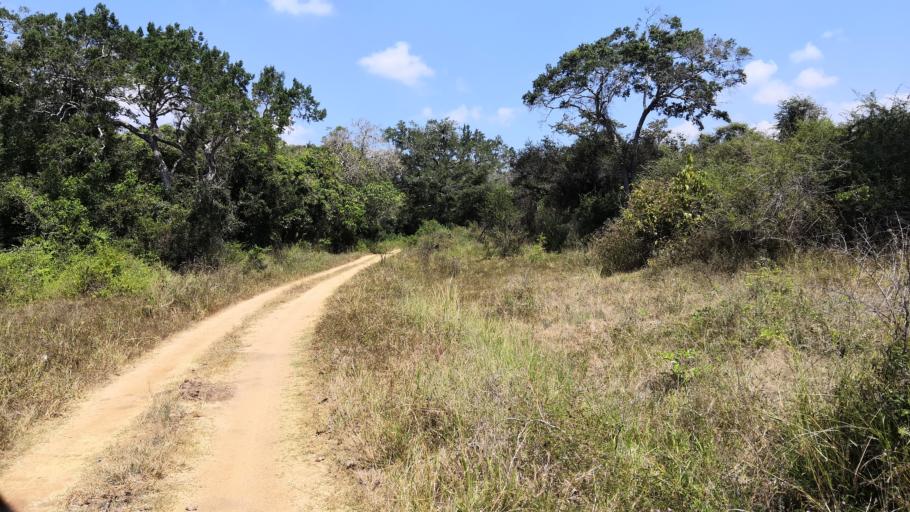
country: LK
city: Padaviya Divisional Secretariat
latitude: 8.9578
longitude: 80.6971
